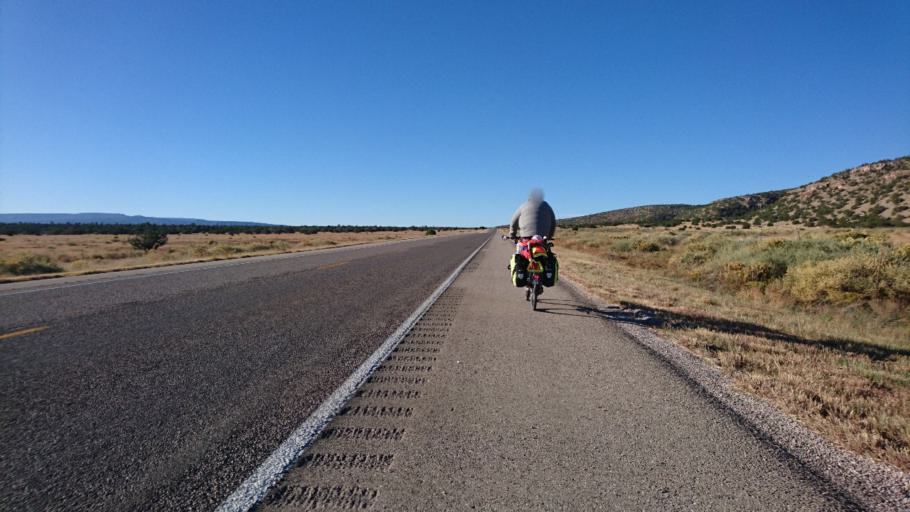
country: US
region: New Mexico
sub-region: Cibola County
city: Grants
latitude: 34.9869
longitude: -107.9029
